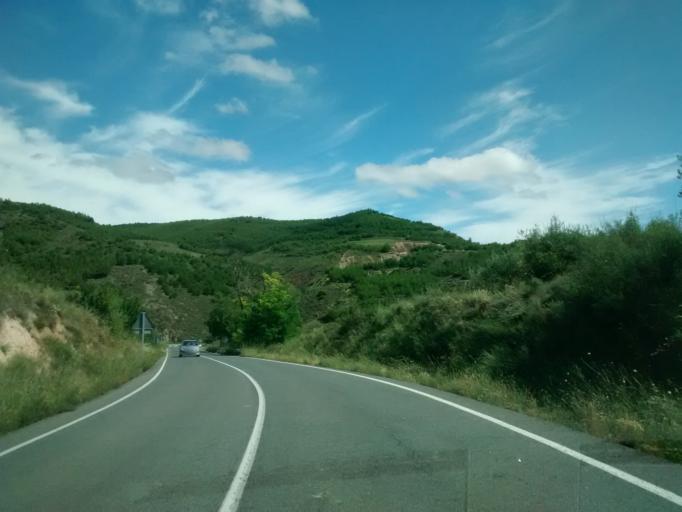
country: ES
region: La Rioja
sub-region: Provincia de La Rioja
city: Leza de Rio Leza
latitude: 42.3436
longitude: -2.4016
